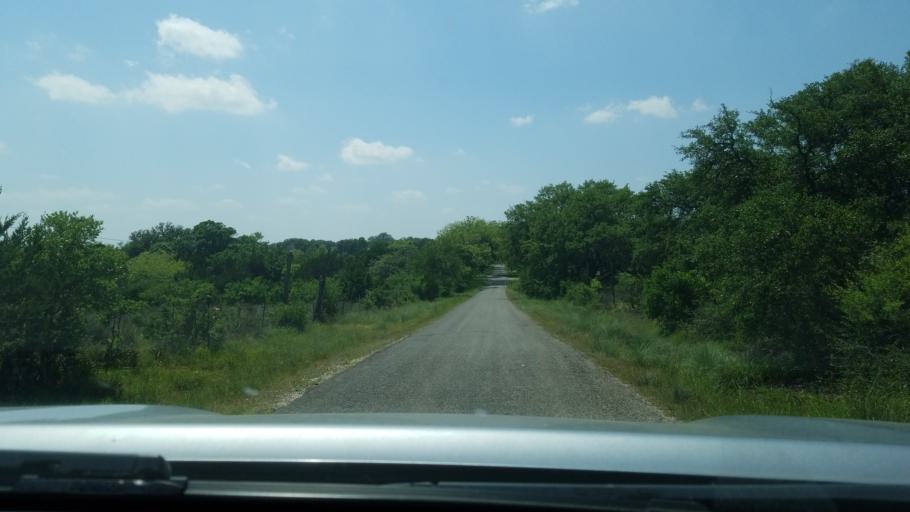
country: US
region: Texas
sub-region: Blanco County
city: Blanco
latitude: 29.9876
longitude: -98.5356
